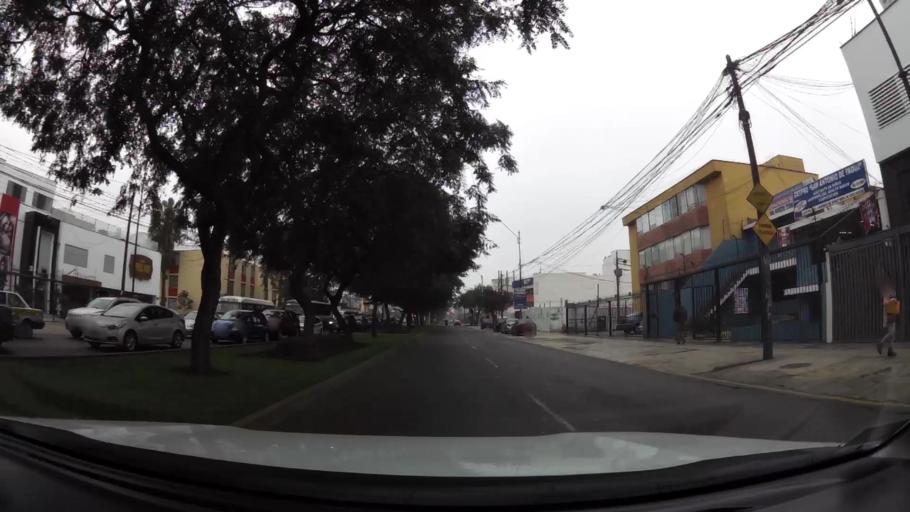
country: PE
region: Lima
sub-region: Lima
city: Surco
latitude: -12.1285
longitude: -76.9948
